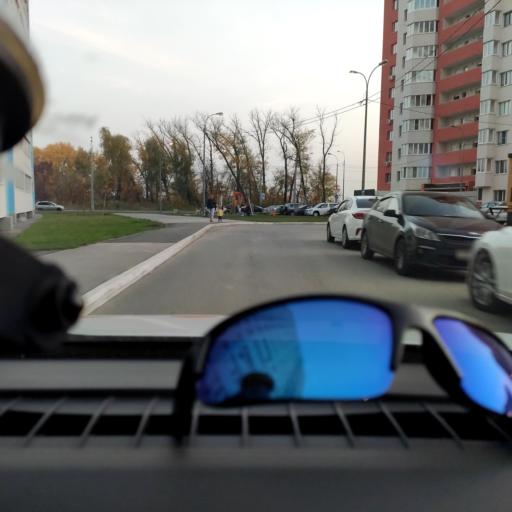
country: RU
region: Samara
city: Samara
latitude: 53.1476
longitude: 50.0787
